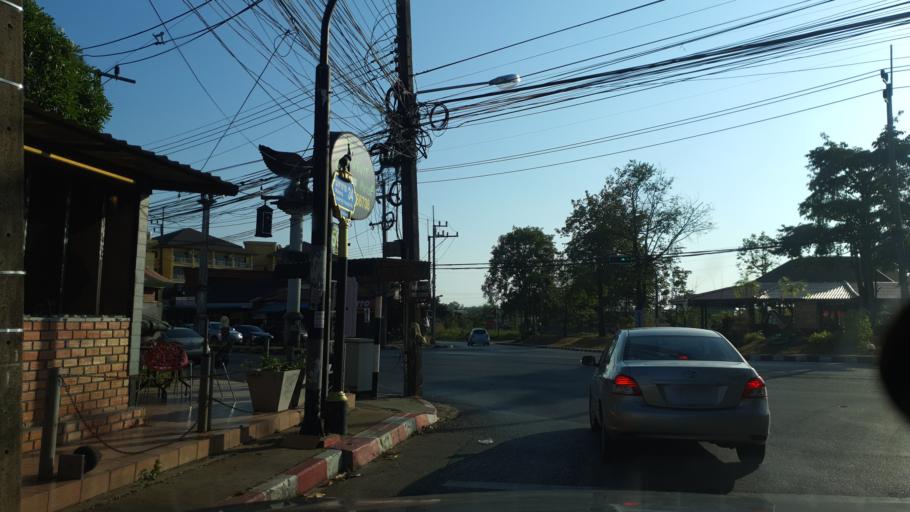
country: TH
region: Krabi
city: Krabi
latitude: 8.0762
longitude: 98.9097
